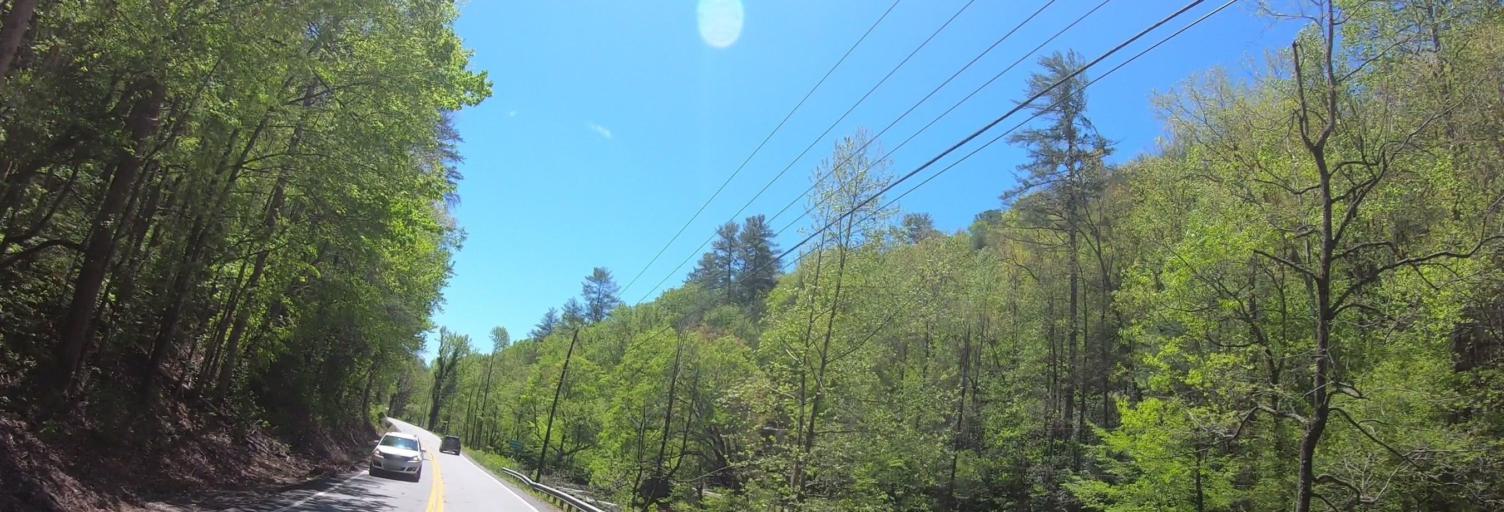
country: US
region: Georgia
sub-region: White County
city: Cleveland
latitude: 34.7178
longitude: -83.7478
